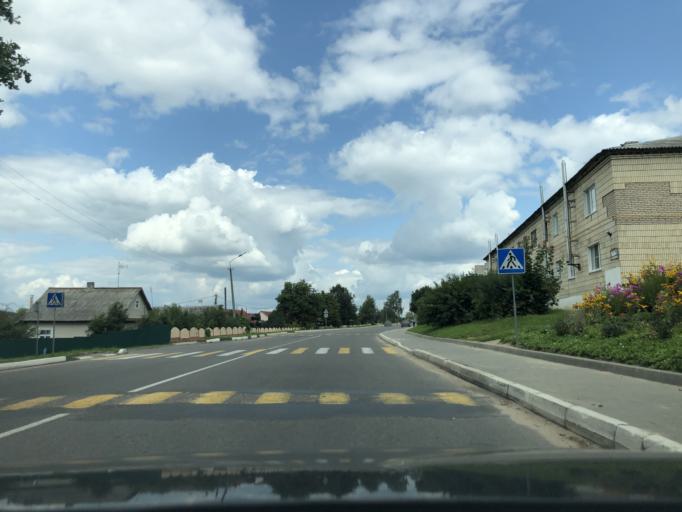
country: BY
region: Minsk
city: Lahoysk
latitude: 54.2069
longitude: 27.8523
